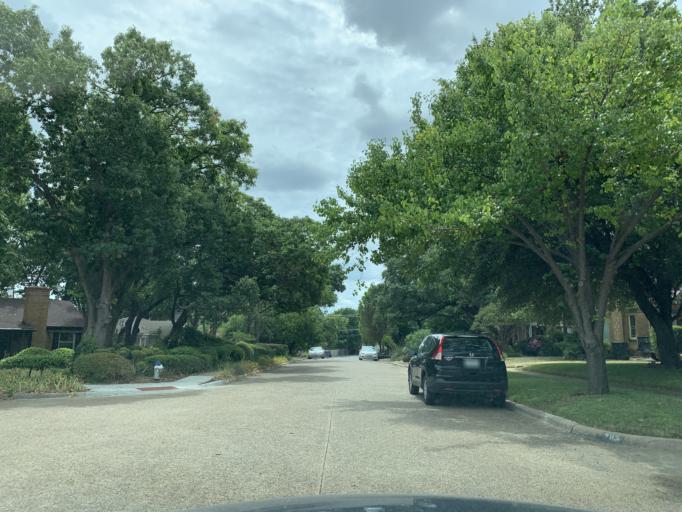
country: US
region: Texas
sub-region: Dallas County
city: Cockrell Hill
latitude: 32.7507
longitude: -96.8664
